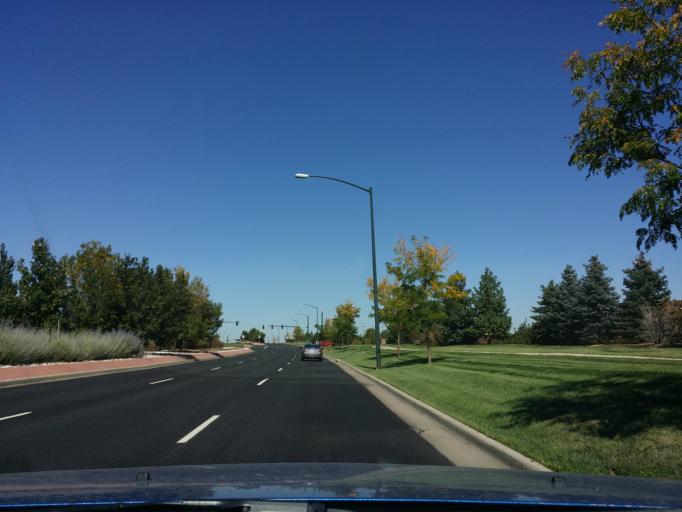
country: US
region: Colorado
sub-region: Adams County
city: Northglenn
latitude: 39.9596
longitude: -104.9966
